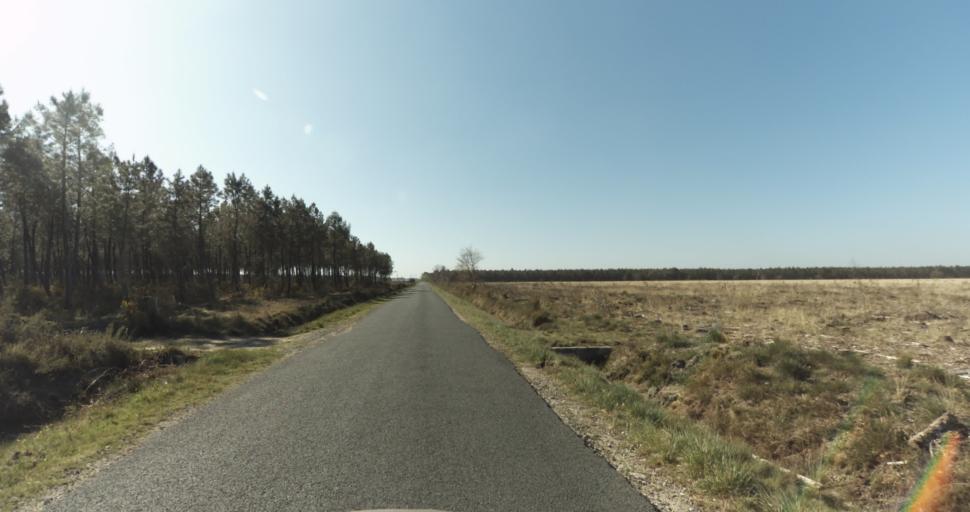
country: FR
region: Aquitaine
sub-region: Departement de la Gironde
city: Marcheprime
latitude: 44.7803
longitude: -0.8605
